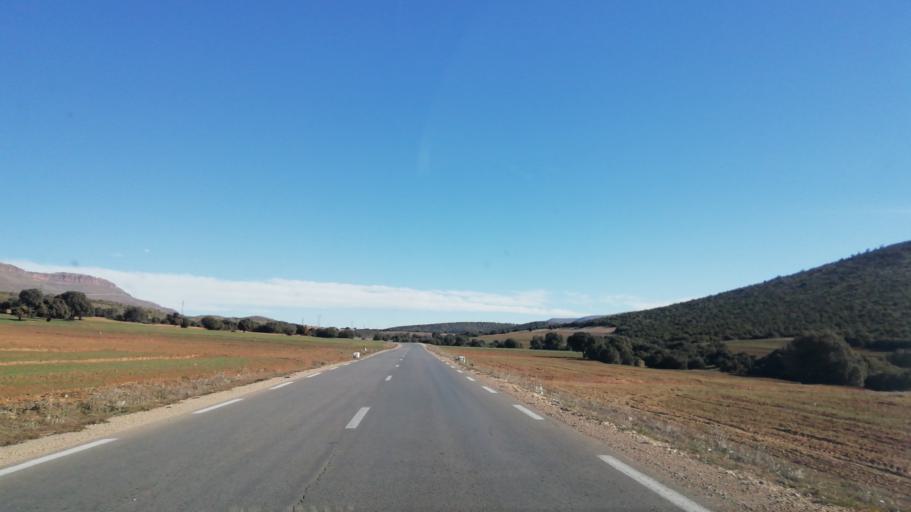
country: DZ
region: Tlemcen
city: Sebdou
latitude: 34.7040
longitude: -1.2200
